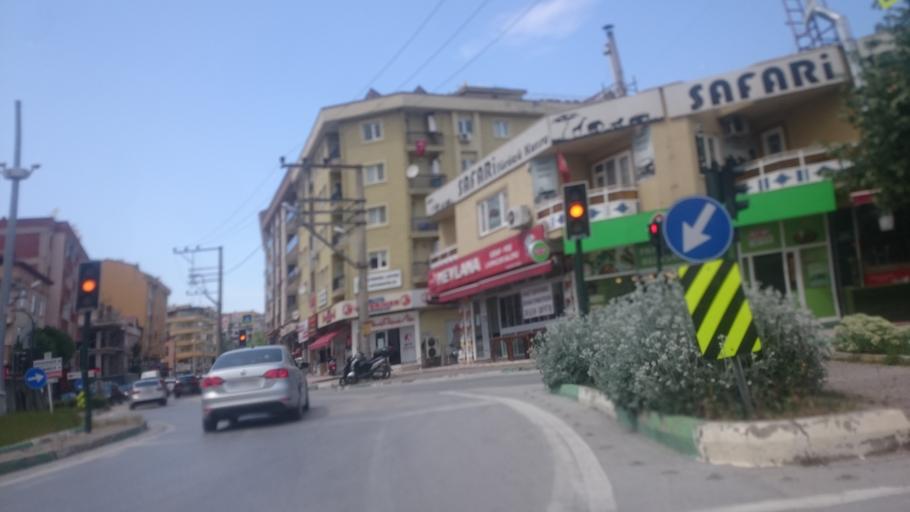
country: TR
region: Bursa
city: Yildirim
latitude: 40.2215
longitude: 28.9890
